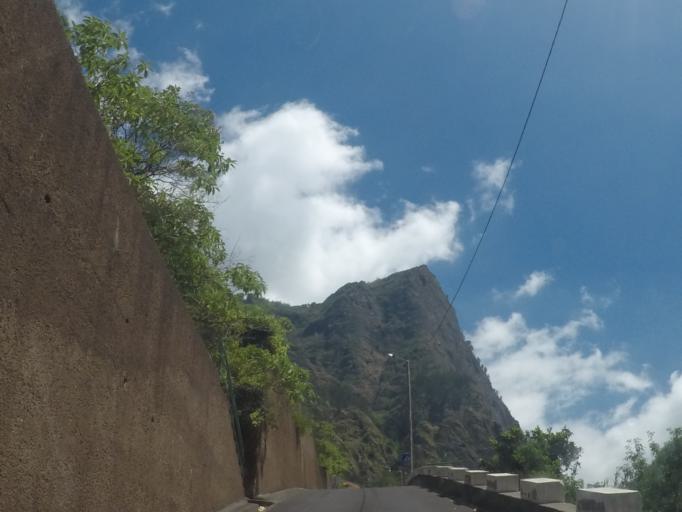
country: PT
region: Madeira
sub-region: Camara de Lobos
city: Curral das Freiras
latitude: 32.7186
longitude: -16.9687
